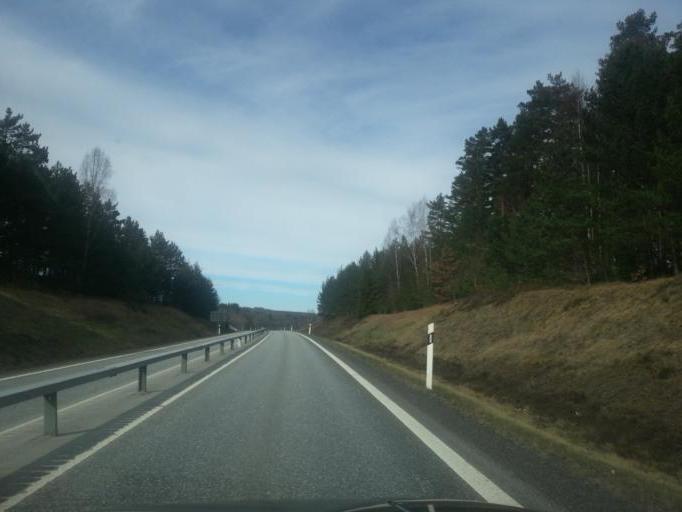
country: SE
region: Joenkoeping
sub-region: Jonkopings Kommun
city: Bankeryd
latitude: 57.8554
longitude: 14.1044
